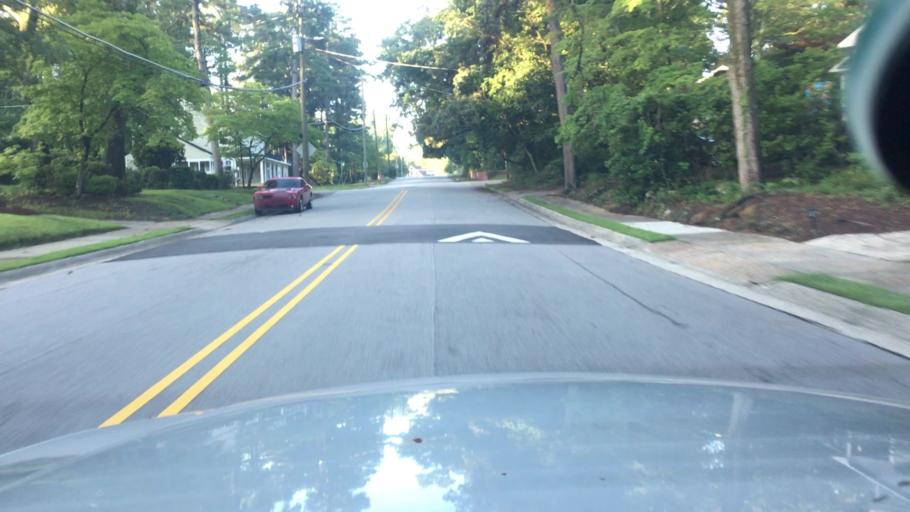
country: US
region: North Carolina
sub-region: Cumberland County
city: Fayetteville
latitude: 35.0632
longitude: -78.9051
